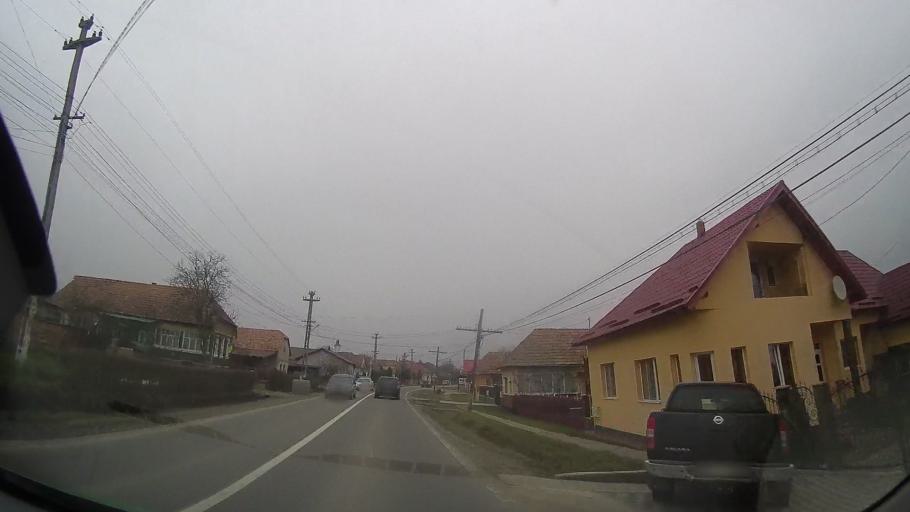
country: RO
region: Mures
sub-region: Comuna Ceausu de Campie
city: Ceausu de Campie
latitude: 46.6120
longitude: 24.5279
